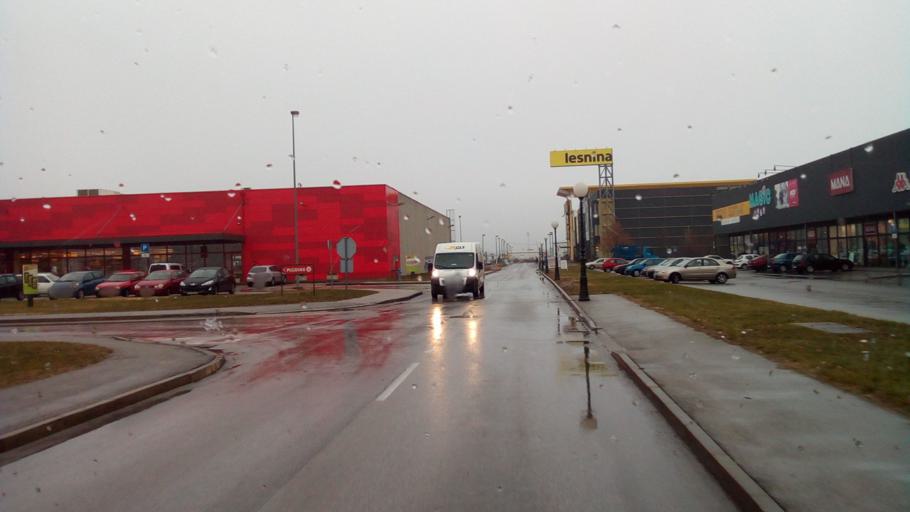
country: HR
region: Varazdinska
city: Varazdin
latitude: 46.2920
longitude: 16.3547
